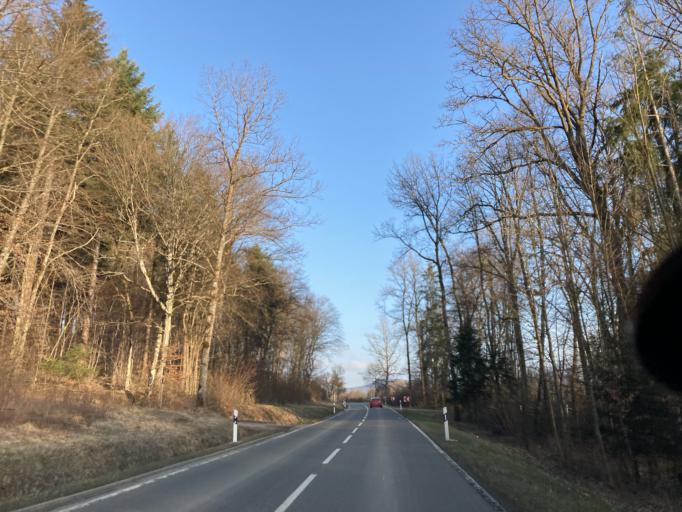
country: DE
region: Baden-Wuerttemberg
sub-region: Tuebingen Region
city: Ofterdingen
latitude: 48.4192
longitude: 9.0030
